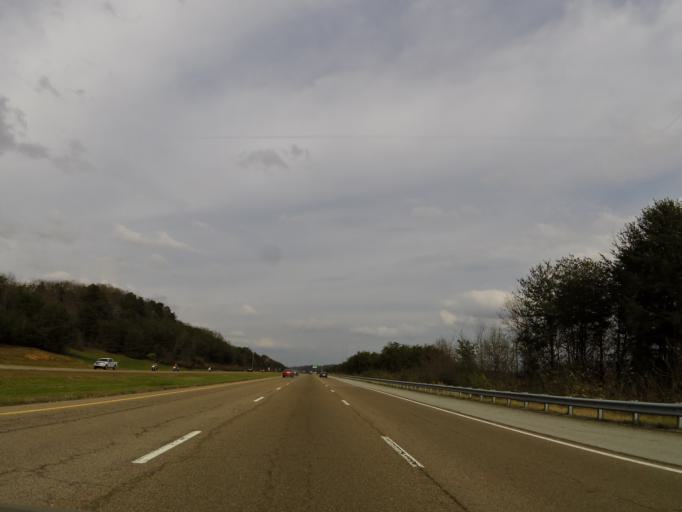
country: US
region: Tennessee
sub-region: Hamilton County
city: Red Bank
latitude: 35.1090
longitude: -85.3094
